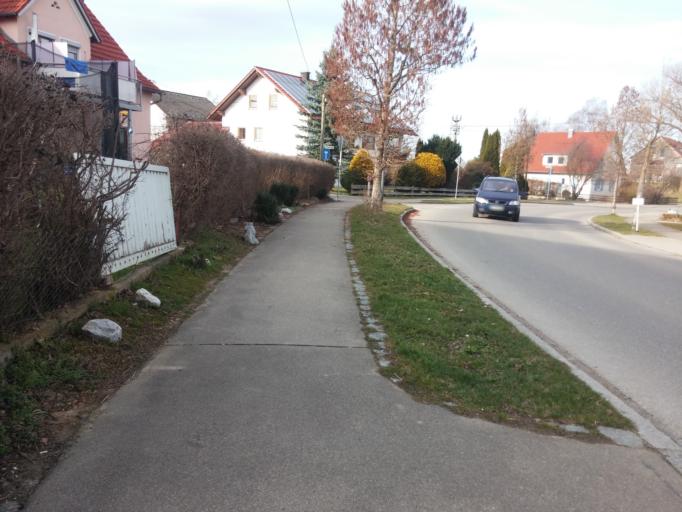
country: DE
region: Bavaria
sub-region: Swabia
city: Holzgunz
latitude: 48.0158
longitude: 10.2475
